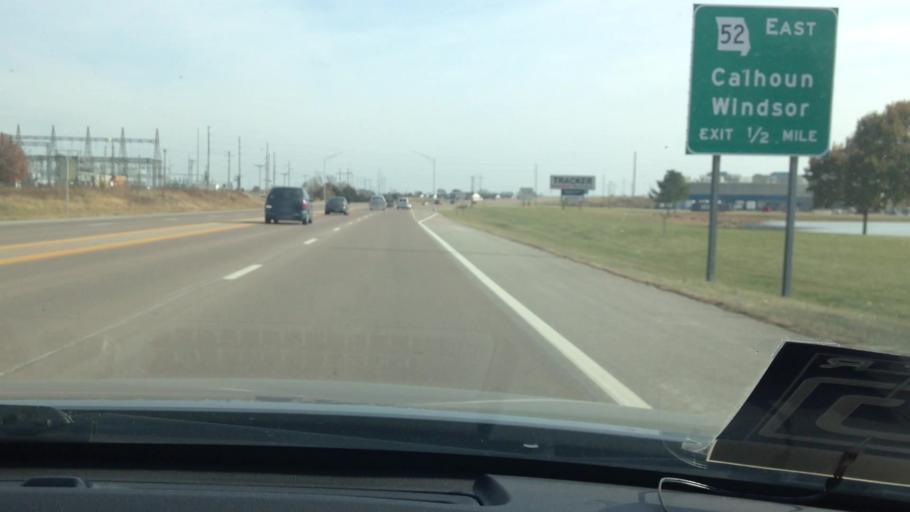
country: US
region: Missouri
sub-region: Henry County
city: Clinton
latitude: 38.3880
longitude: -93.7641
